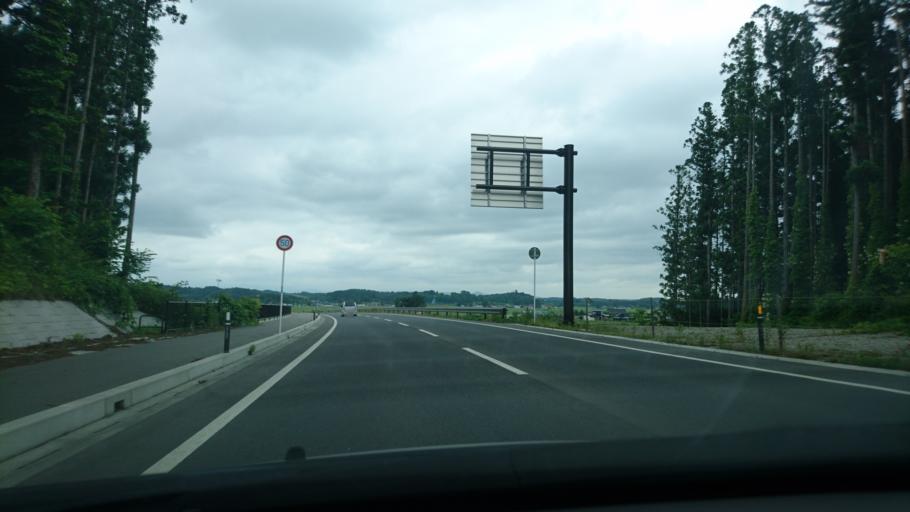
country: JP
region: Miyagi
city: Furukawa
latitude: 38.7437
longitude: 141.0383
